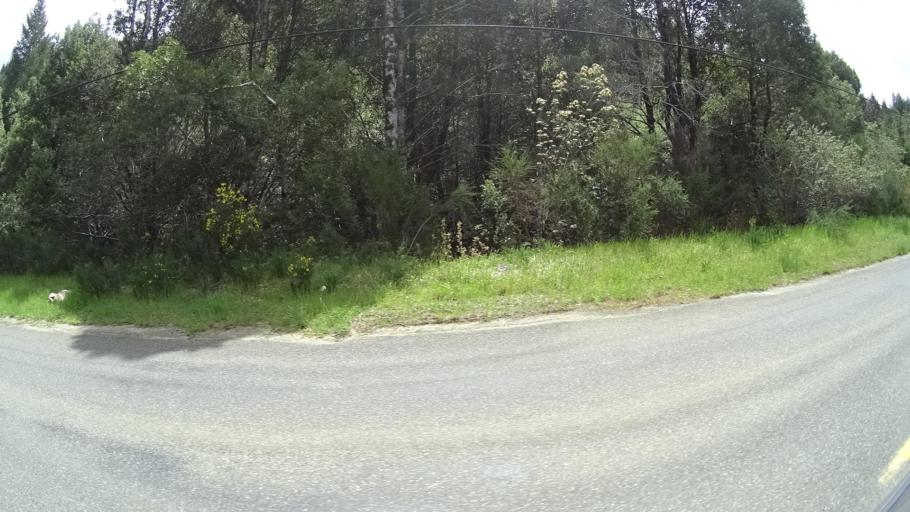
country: US
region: California
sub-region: Humboldt County
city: Redway
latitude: 40.0769
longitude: -123.9563
